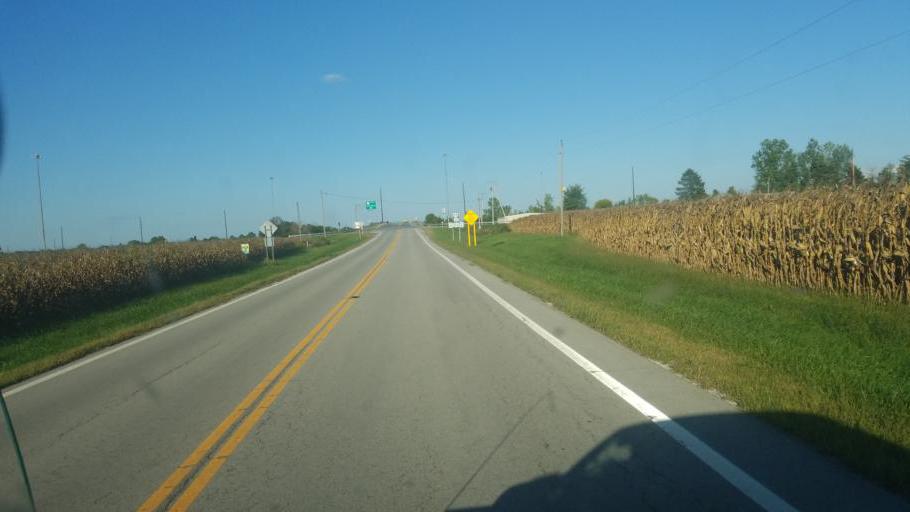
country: US
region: Ohio
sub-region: Wyandot County
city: Carey
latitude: 40.9385
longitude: -83.4045
